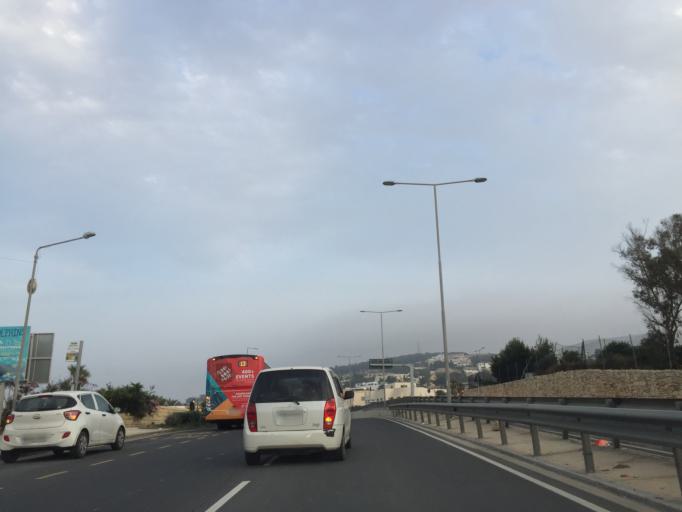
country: MT
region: Hal Gharghur
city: Hal Gharghur
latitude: 35.9388
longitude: 14.4562
